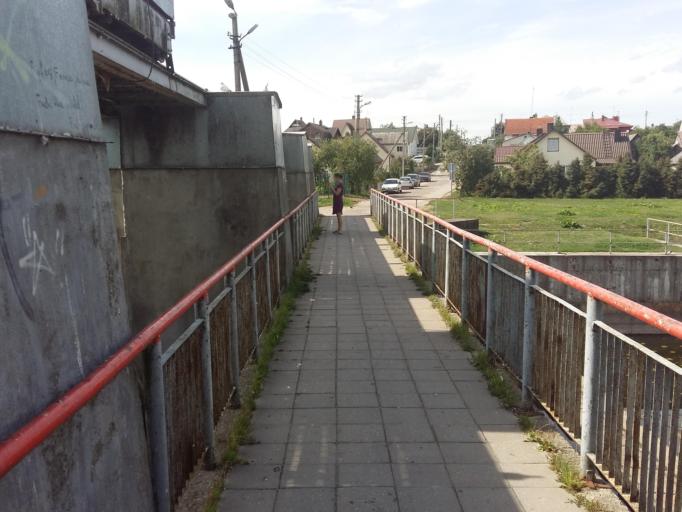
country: LT
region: Marijampoles apskritis
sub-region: Marijampole Municipality
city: Marijampole
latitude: 54.5555
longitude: 23.3414
